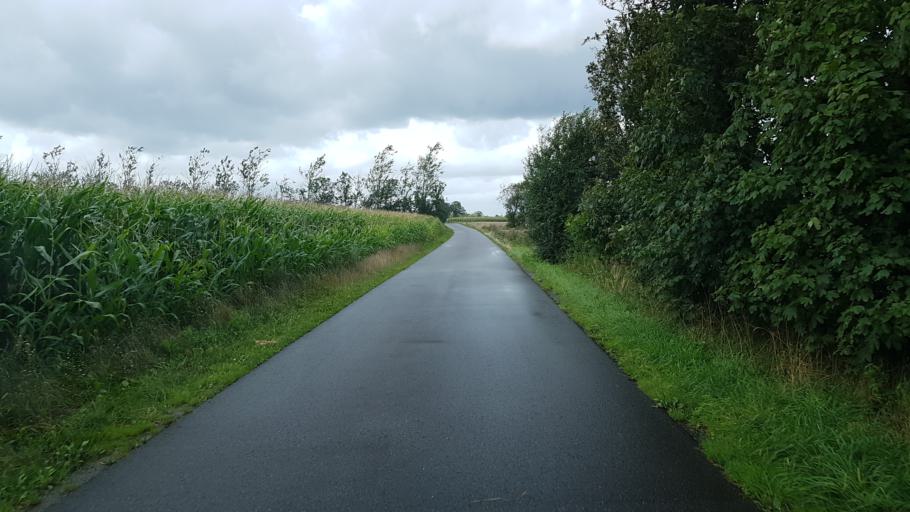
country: DK
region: South Denmark
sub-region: Vejen Kommune
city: Holsted
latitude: 55.5979
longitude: 8.8608
